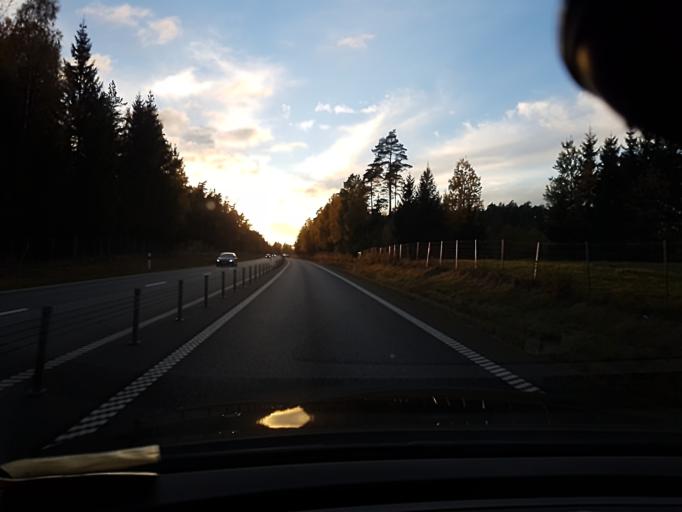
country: SE
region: Kronoberg
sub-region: Ljungby Kommun
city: Ljungby
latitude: 56.8514
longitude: 13.9994
